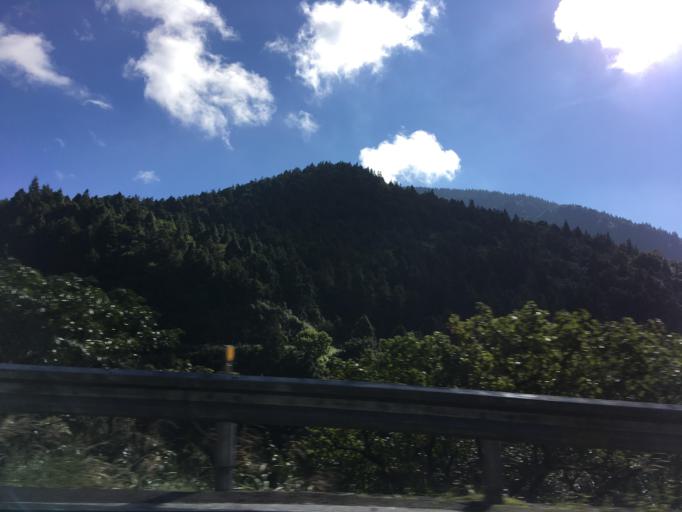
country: TW
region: Taiwan
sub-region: Yilan
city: Yilan
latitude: 24.5043
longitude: 121.5532
